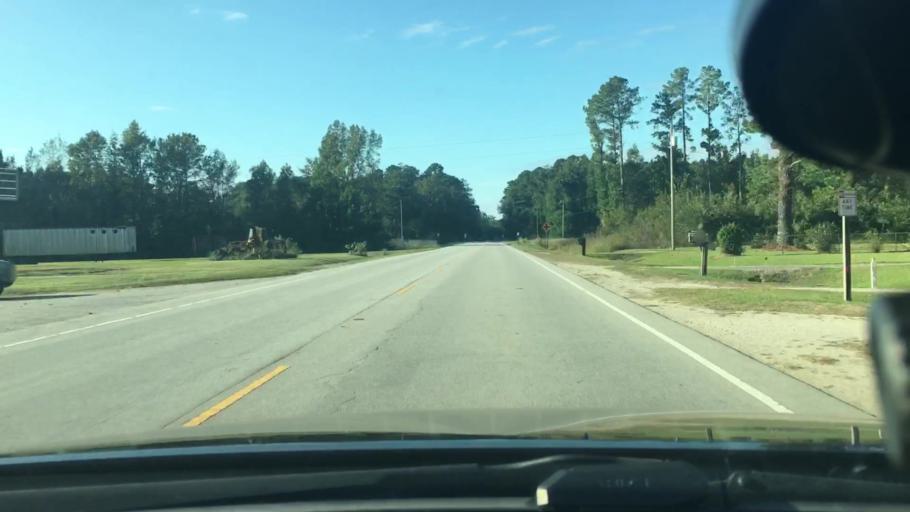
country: US
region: North Carolina
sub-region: Craven County
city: Vanceboro
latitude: 35.3169
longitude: -77.1428
